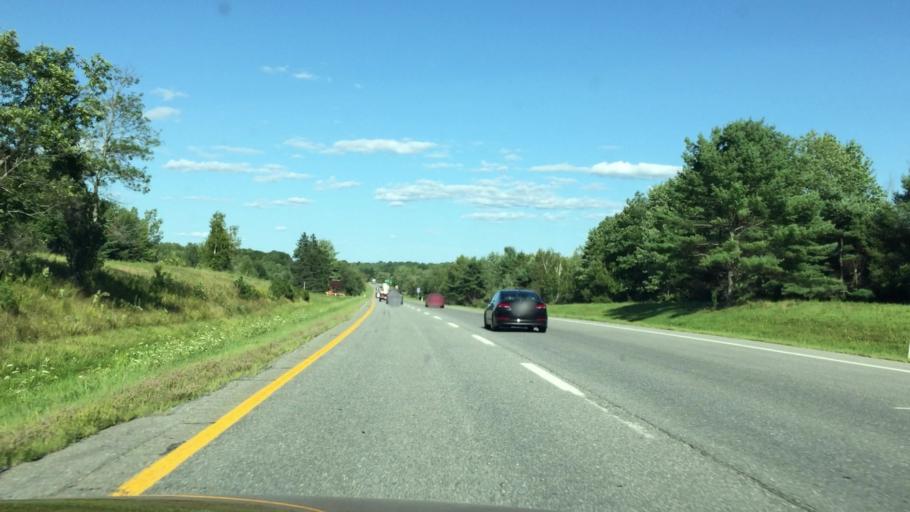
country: US
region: Maine
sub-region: Penobscot County
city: Hermon
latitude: 44.7587
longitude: -68.9681
